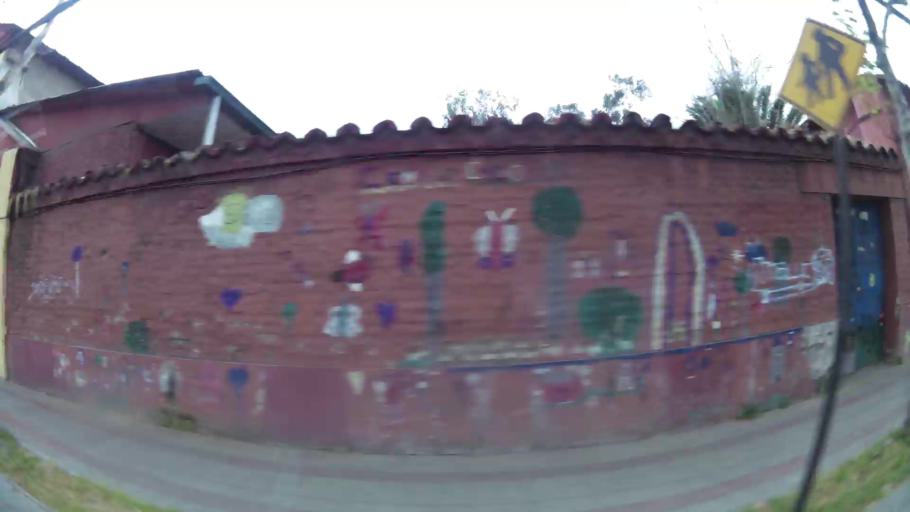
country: CL
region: Santiago Metropolitan
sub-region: Provincia de Santiago
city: Santiago
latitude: -33.4355
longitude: -70.6227
